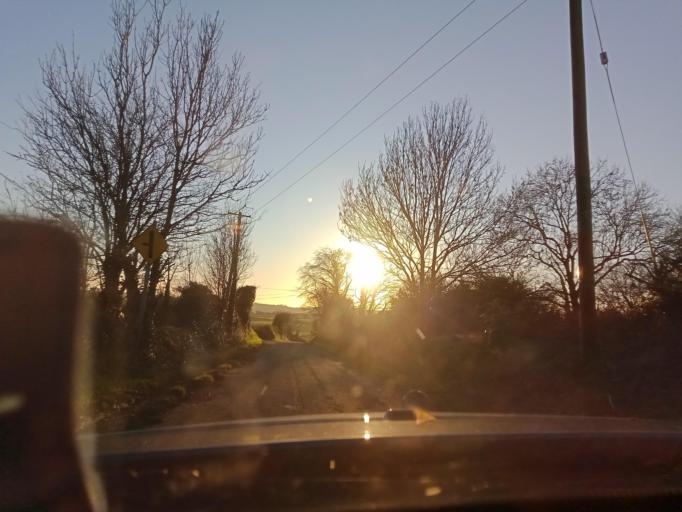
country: IE
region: Leinster
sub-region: Loch Garman
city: New Ross
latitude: 52.3762
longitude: -7.0144
